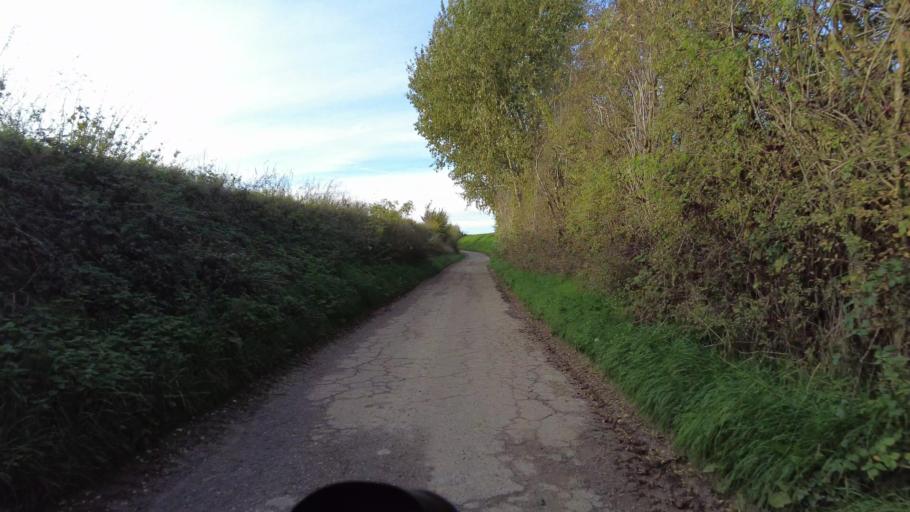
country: BE
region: Flanders
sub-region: Provincie Vlaams-Brabant
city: Hoegaarden
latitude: 50.7556
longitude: 4.9320
